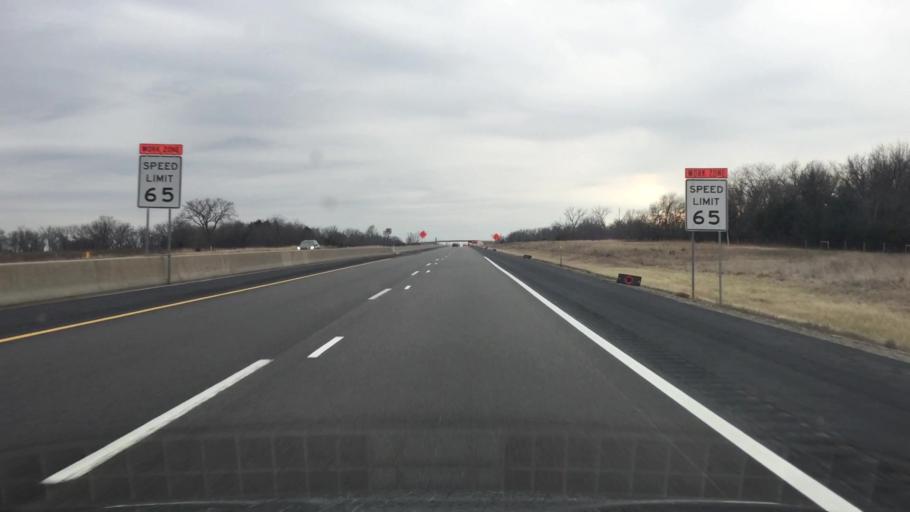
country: US
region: Kansas
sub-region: Osage County
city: Osage City
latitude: 38.7049
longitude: -95.9863
